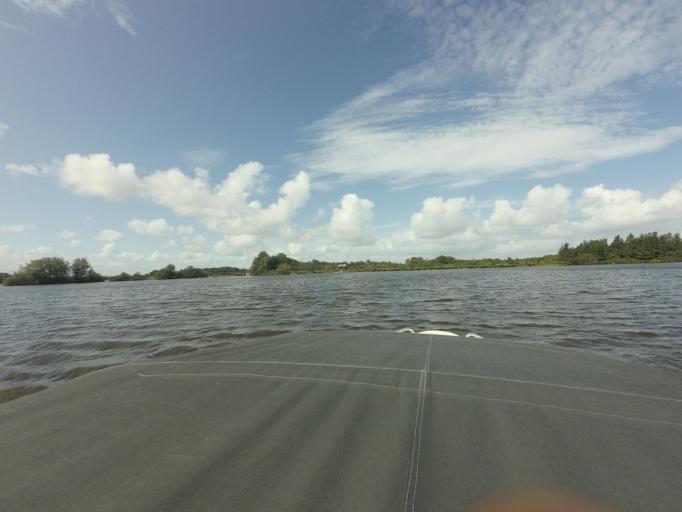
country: NL
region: Friesland
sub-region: Gemeente Boarnsterhim
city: Warten
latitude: 53.1157
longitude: 5.9296
